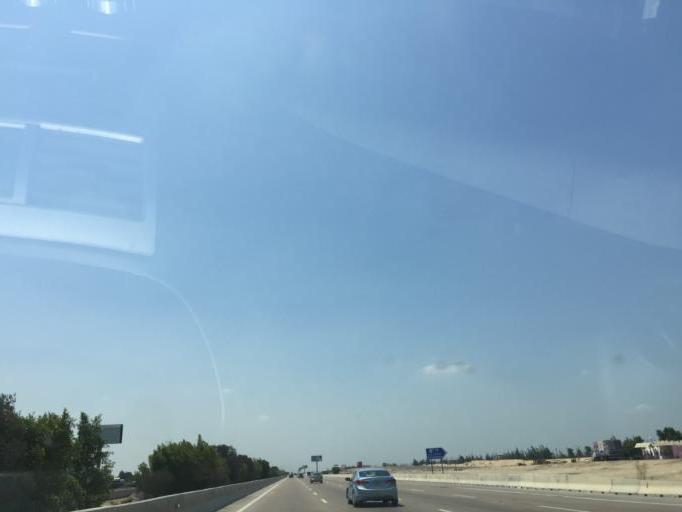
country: EG
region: Al Buhayrah
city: Beheira
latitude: 30.4462
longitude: 30.3220
